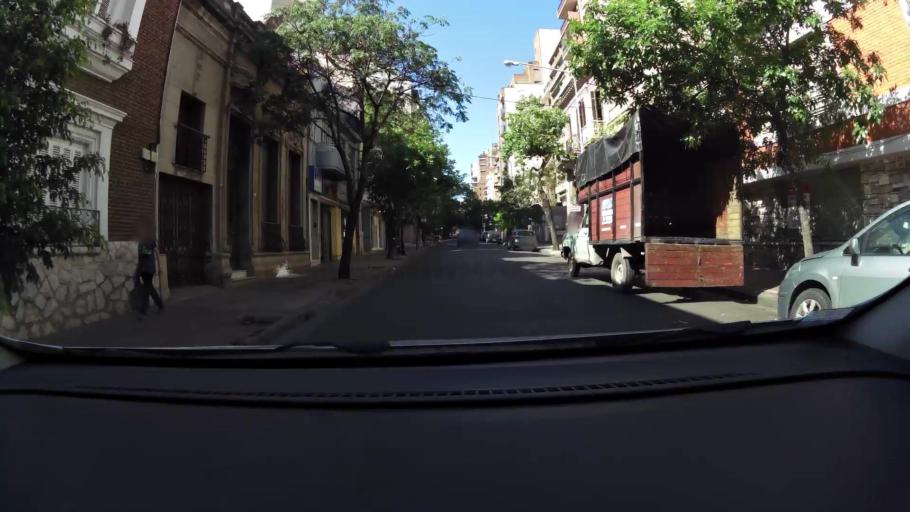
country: AR
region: Cordoba
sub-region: Departamento de Capital
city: Cordoba
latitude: -31.4233
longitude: -64.1841
